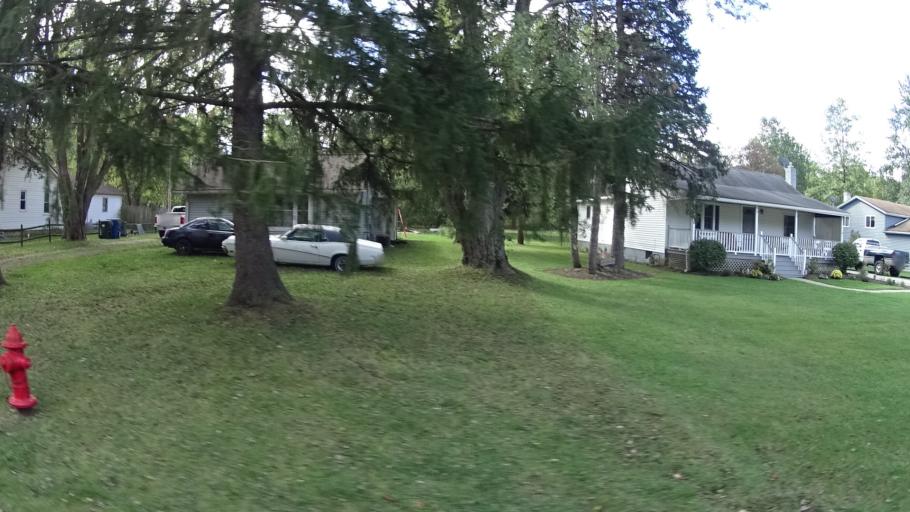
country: US
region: Ohio
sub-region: Lorain County
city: Grafton
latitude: 41.2823
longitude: -82.0561
